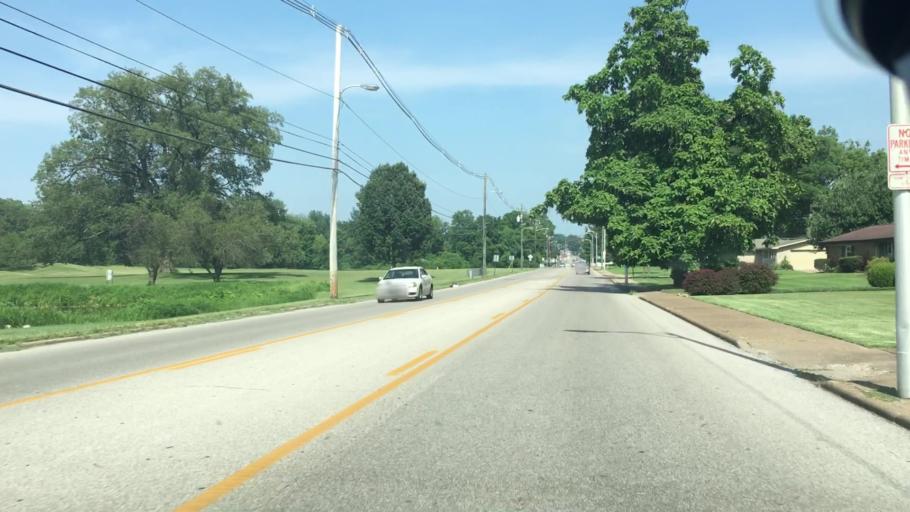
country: US
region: Indiana
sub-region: Vanderburgh County
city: Evansville
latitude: 37.9697
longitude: -87.5035
